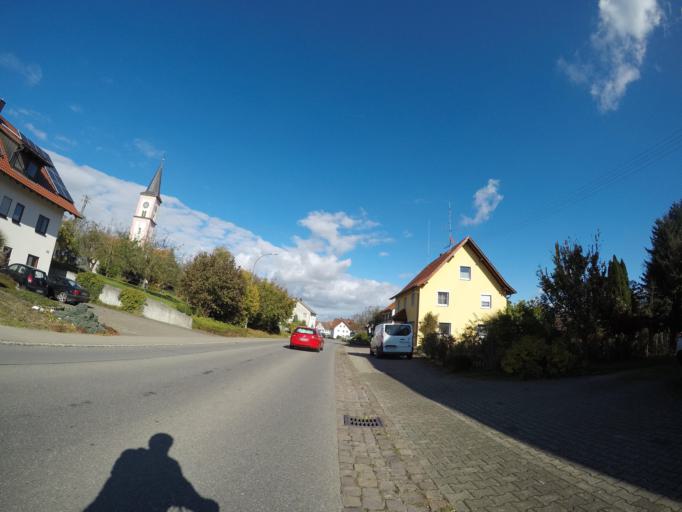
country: DE
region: Baden-Wuerttemberg
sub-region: Tuebingen Region
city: Grundsheim
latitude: 48.1467
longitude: 9.6653
